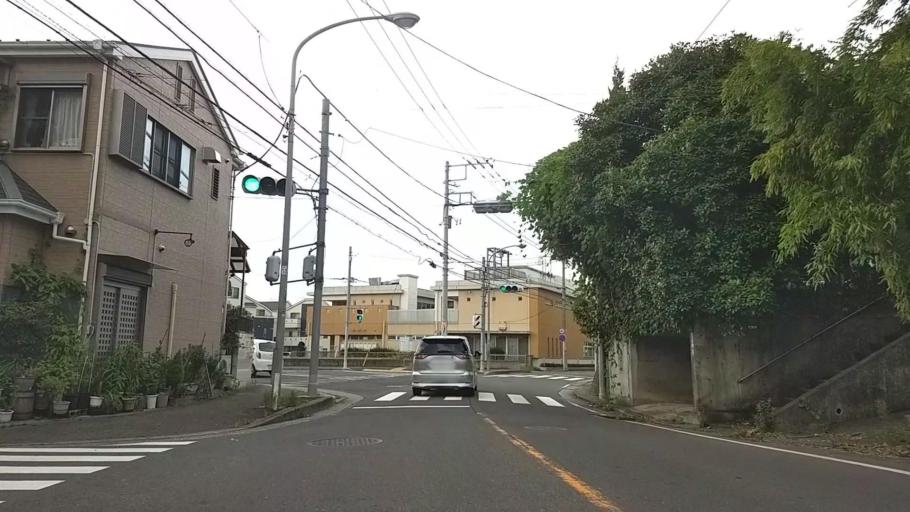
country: JP
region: Kanagawa
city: Yokohama
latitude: 35.5036
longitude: 139.5636
